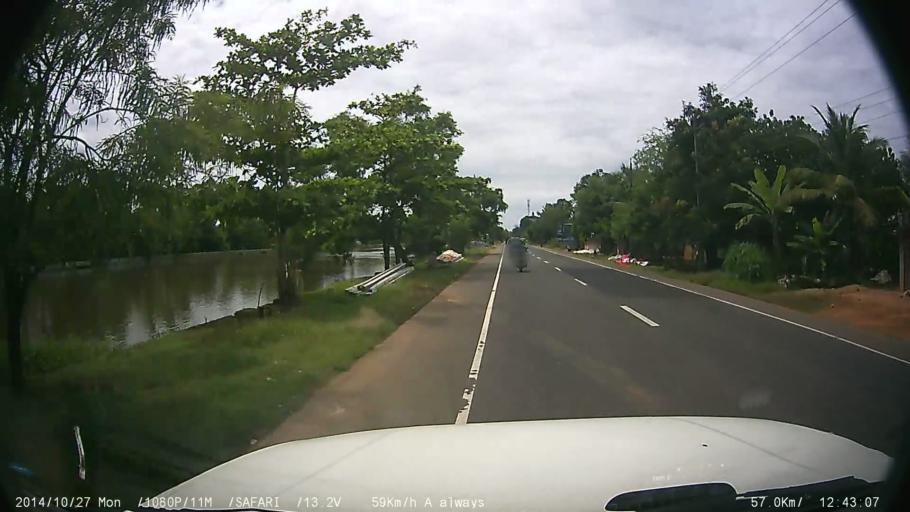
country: IN
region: Kerala
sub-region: Kottayam
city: Changanacheri
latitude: 9.4228
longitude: 76.5018
